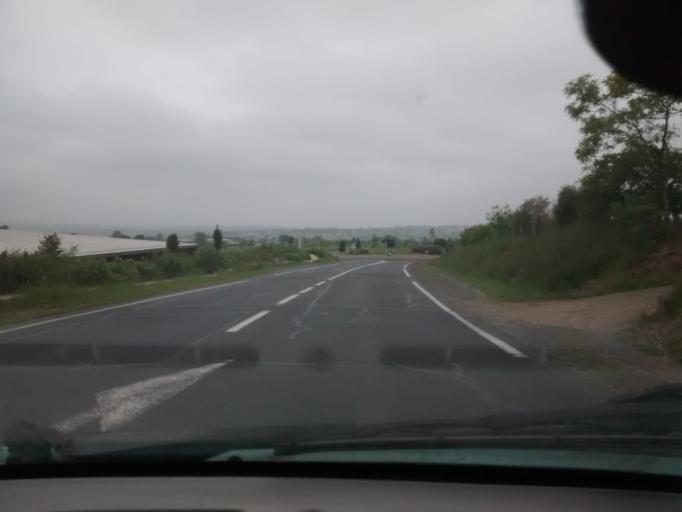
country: FR
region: Lower Normandy
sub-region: Departement de la Manche
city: Torigni-sur-Vire
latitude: 49.0480
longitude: -1.0004
